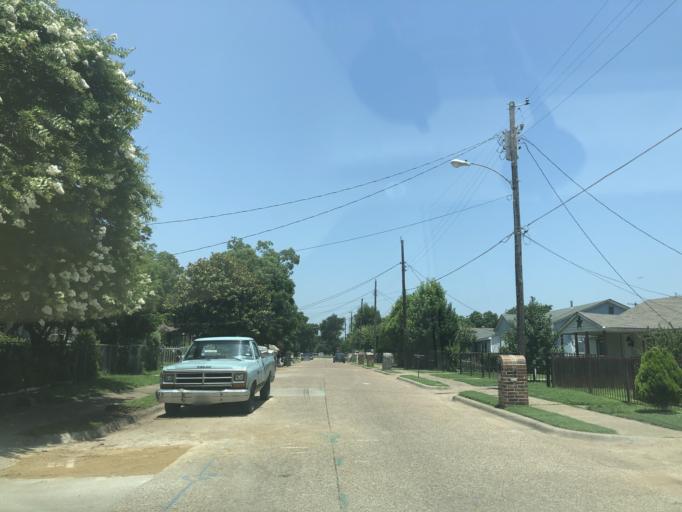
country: US
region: Texas
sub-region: Dallas County
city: Dallas
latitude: 32.7798
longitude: -96.8369
